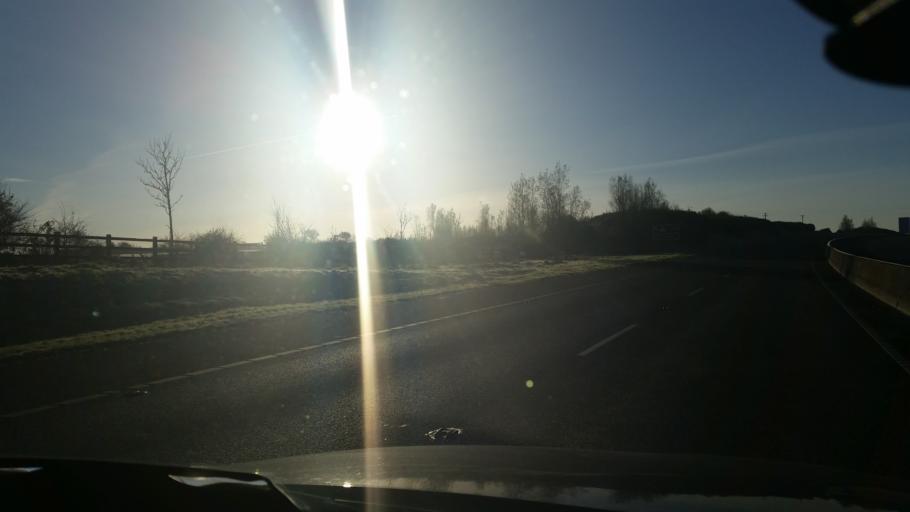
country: IE
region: Leinster
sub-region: Loch Garman
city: Gorey
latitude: 52.6761
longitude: -6.2577
